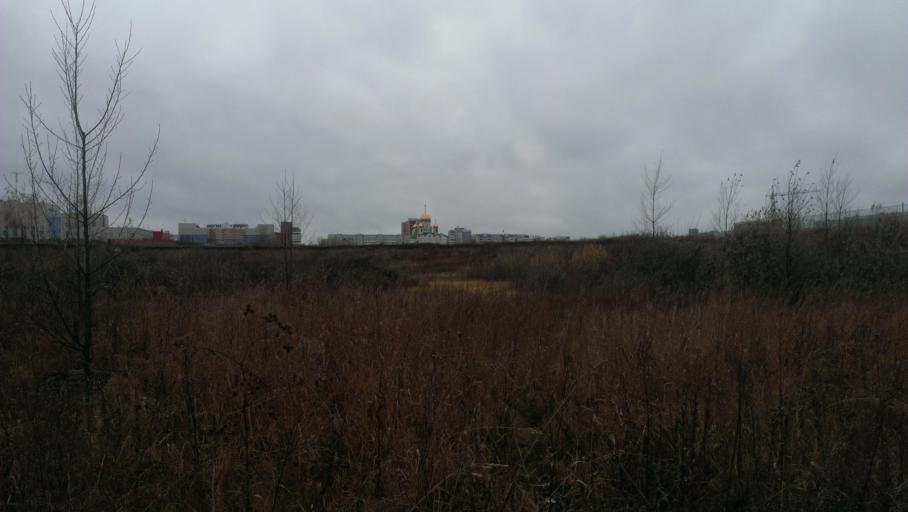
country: RU
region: Altai Krai
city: Novosilikatnyy
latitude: 53.3412
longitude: 83.6847
